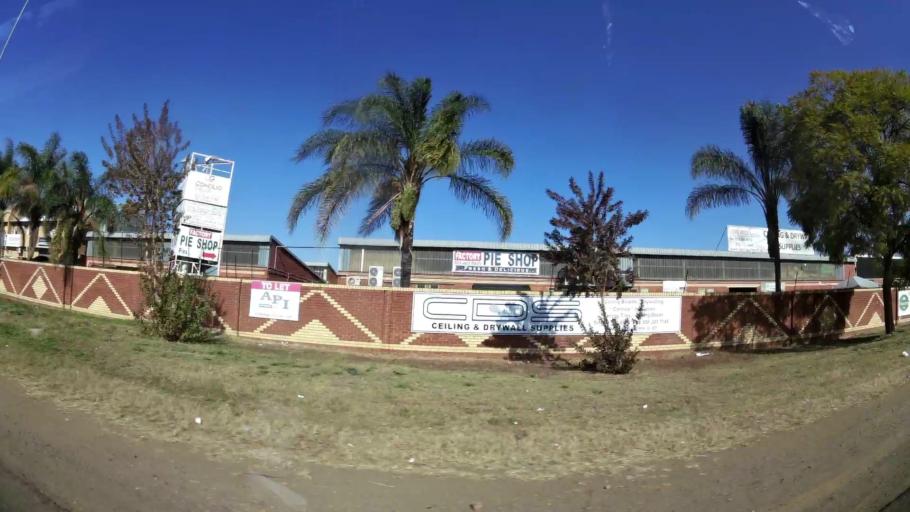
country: ZA
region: Gauteng
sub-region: City of Tshwane Metropolitan Municipality
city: Pretoria
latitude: -25.7177
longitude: 28.2445
